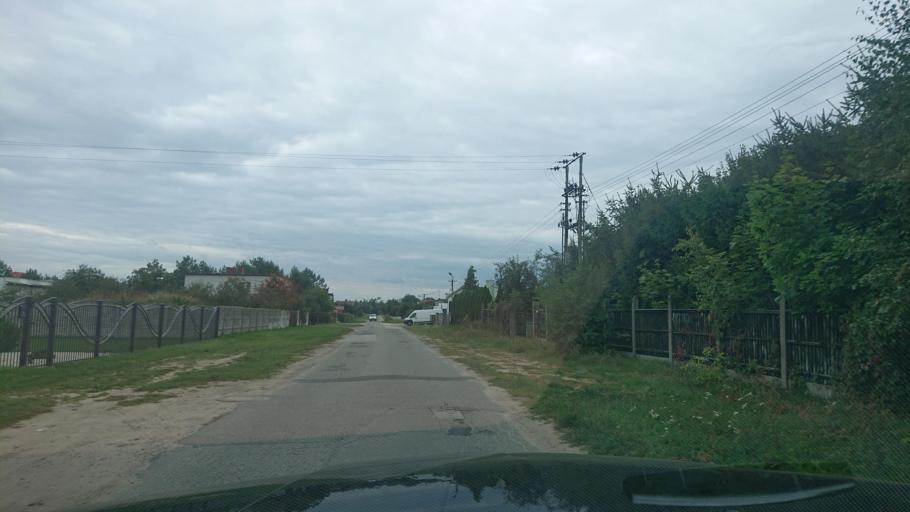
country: PL
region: Greater Poland Voivodeship
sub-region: Powiat gnieznienski
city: Gniezno
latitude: 52.4824
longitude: 17.6019
